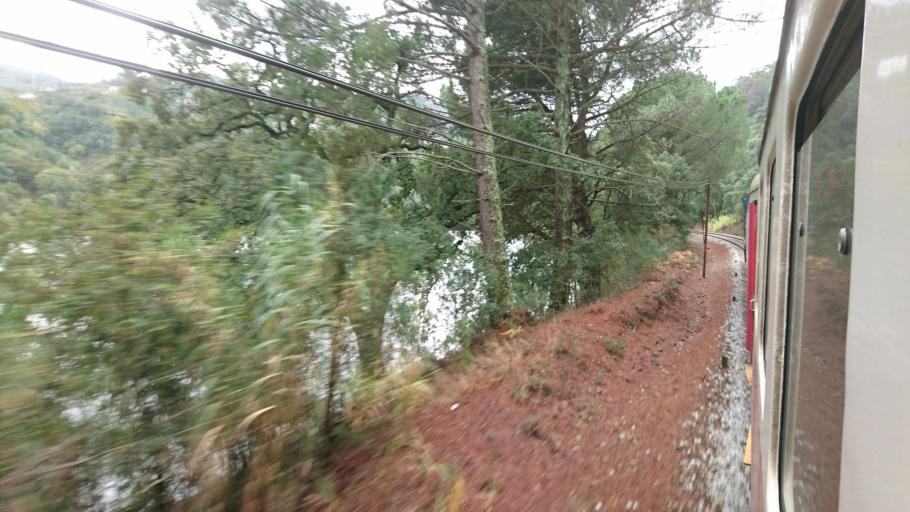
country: PT
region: Viseu
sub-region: Cinfaes
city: Cinfaes
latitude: 41.0939
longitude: -8.0438
